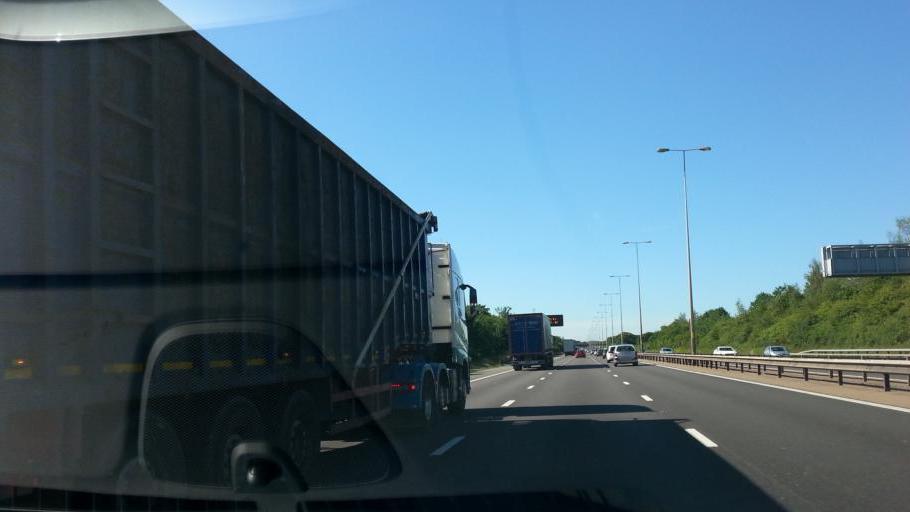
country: GB
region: England
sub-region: Worcestershire
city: Kempsey
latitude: 52.1472
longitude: -2.1929
